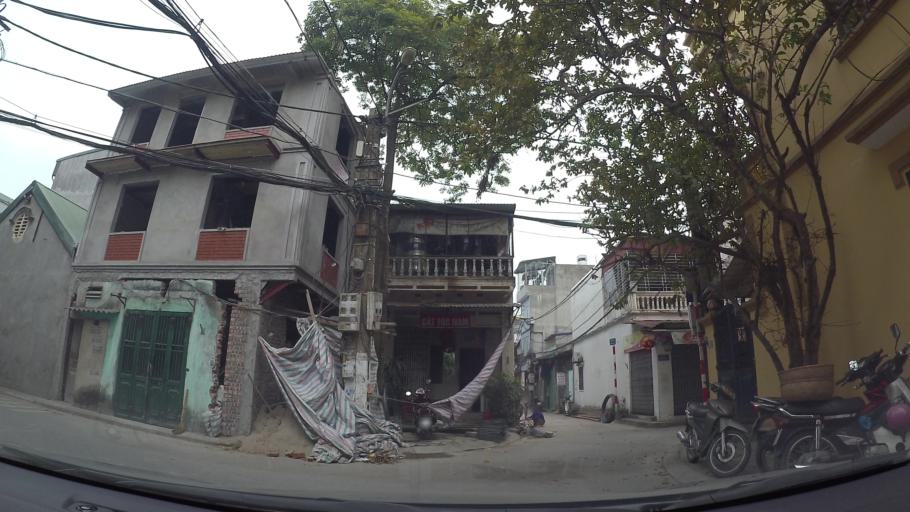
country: VN
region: Ha Noi
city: Trau Quy
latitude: 21.0718
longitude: 105.9060
